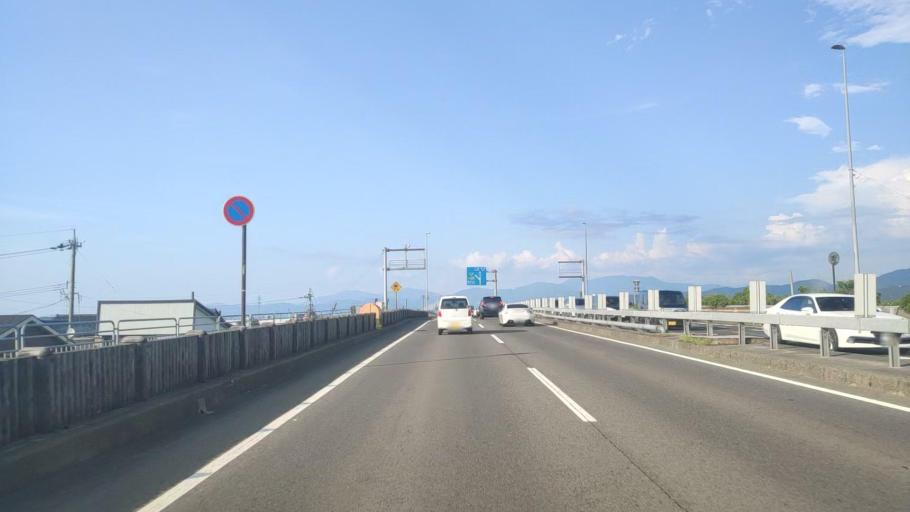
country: JP
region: Fukui
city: Fukui-shi
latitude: 36.0460
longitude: 136.2375
